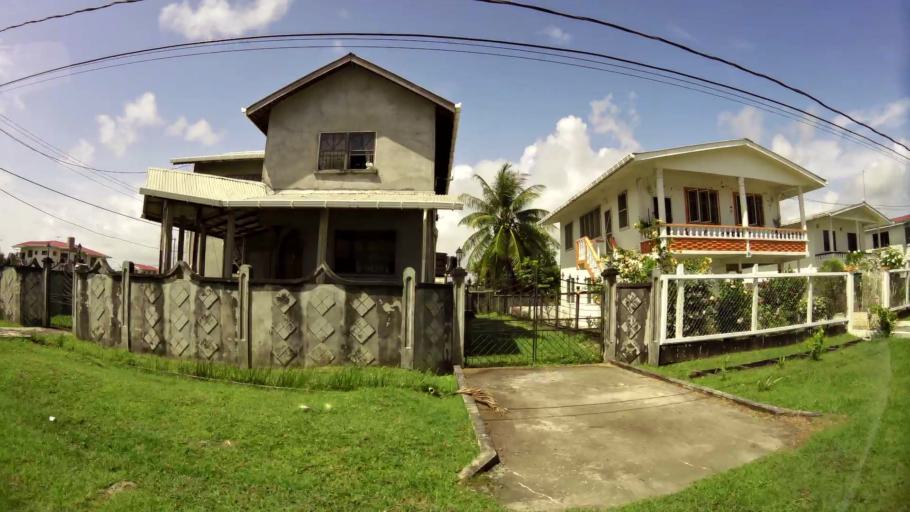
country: GY
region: Demerara-Mahaica
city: Mahaica Village
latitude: 6.7714
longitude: -58.0091
